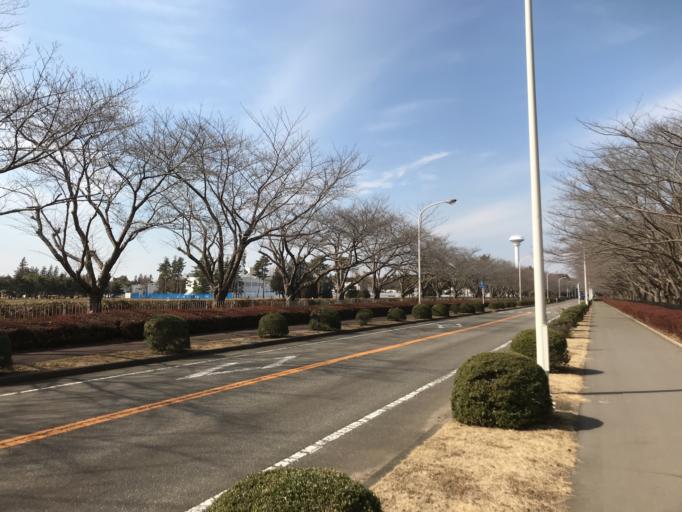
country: JP
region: Ibaraki
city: Naka
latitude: 36.0280
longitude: 140.1073
